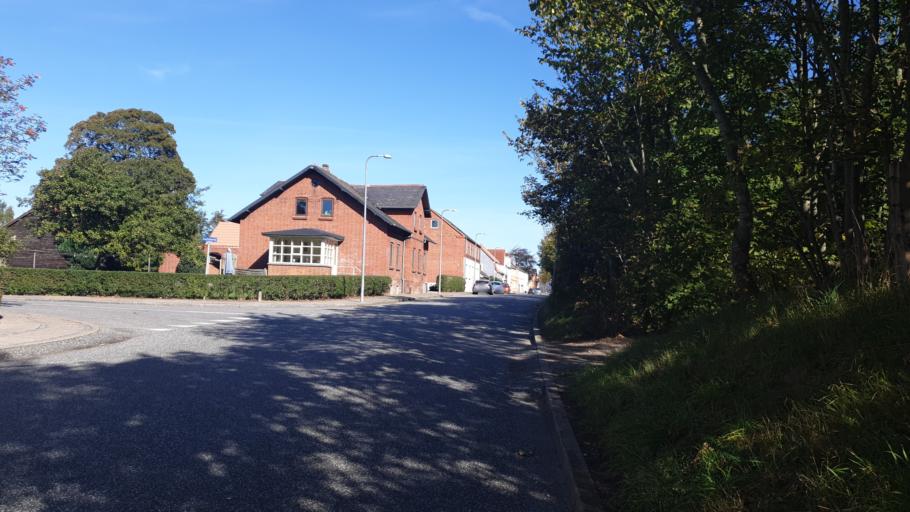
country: DK
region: Central Jutland
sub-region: Hedensted Kommune
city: Hedensted
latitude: 55.8013
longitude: 9.7008
